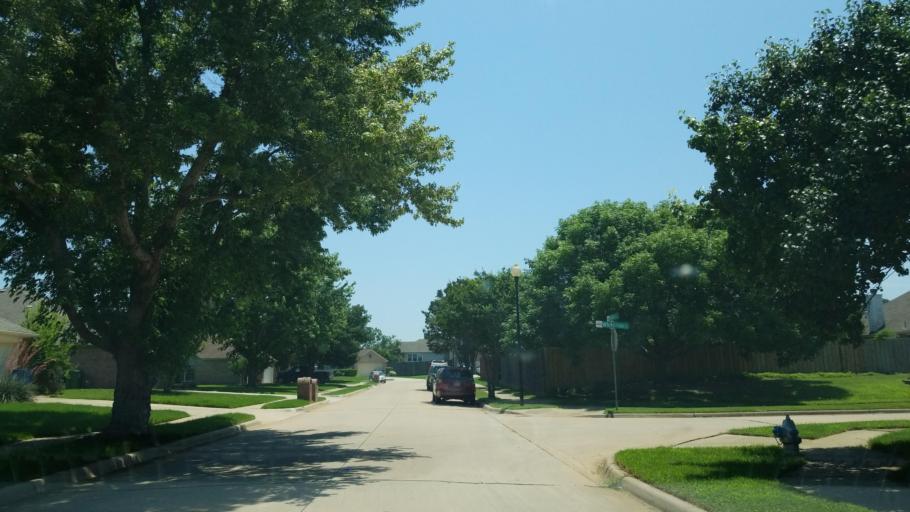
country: US
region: Texas
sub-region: Denton County
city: Hickory Creek
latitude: 33.1385
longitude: -97.0366
